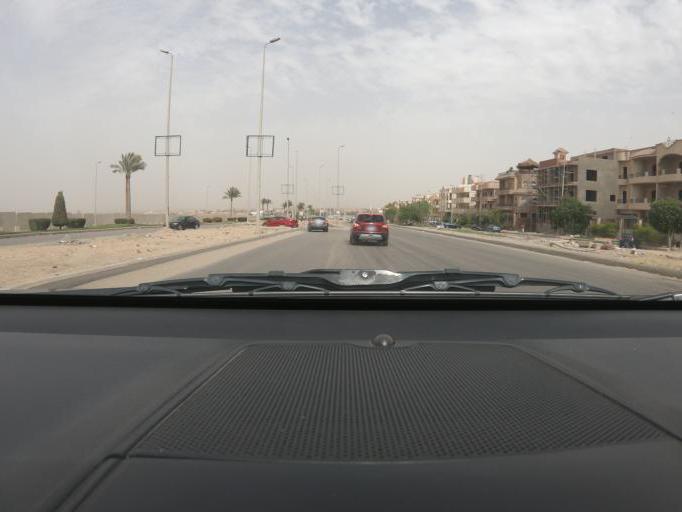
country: EG
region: Muhafazat al Qahirah
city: Cairo
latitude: 30.0264
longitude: 31.4139
